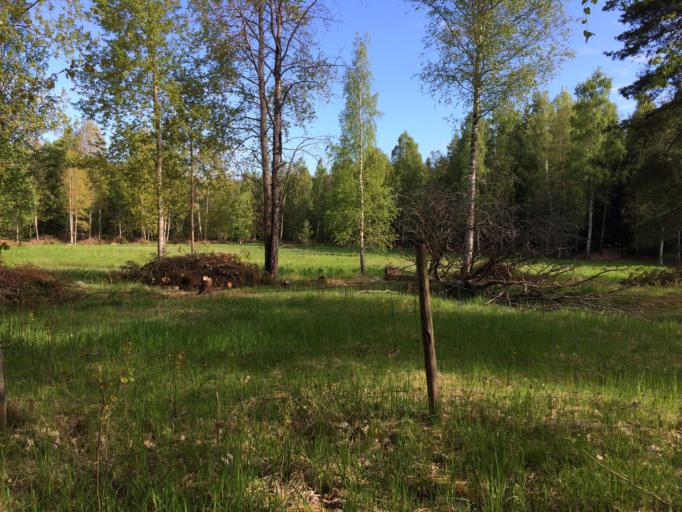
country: SE
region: Vaestmanland
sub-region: Hallstahammars Kommun
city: Hallstahammar
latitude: 59.6101
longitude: 16.2600
